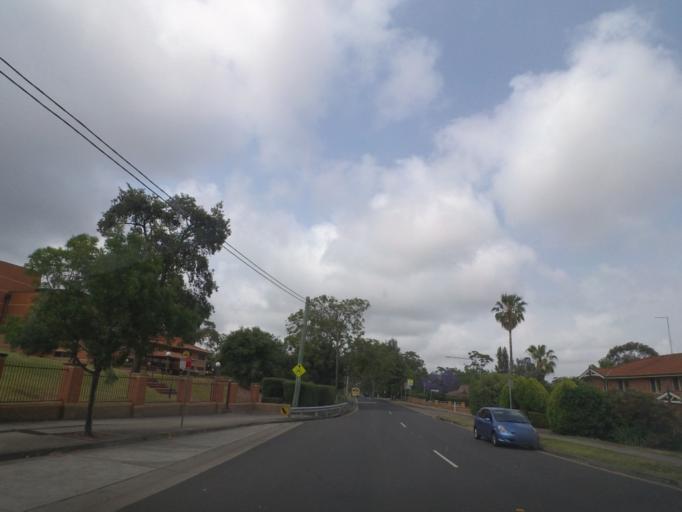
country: AU
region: New South Wales
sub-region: The Hills Shire
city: West Pennant
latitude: -33.7346
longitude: 151.0367
